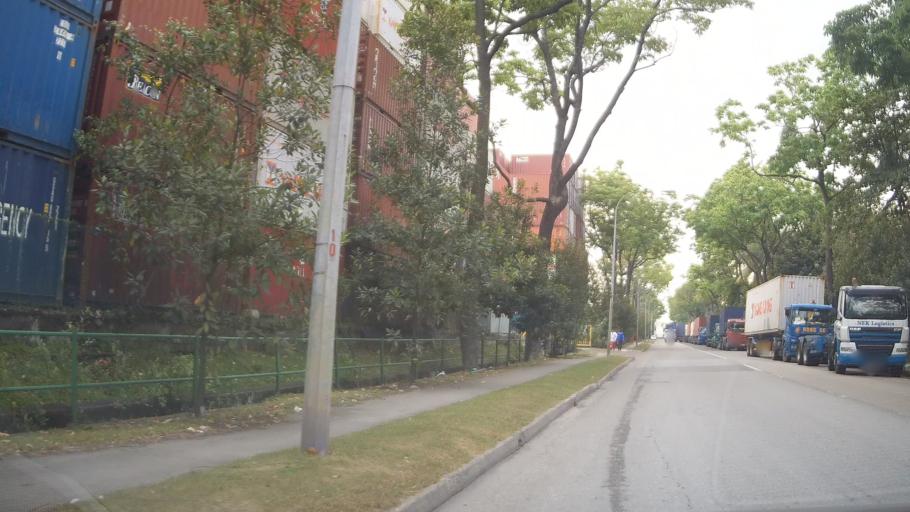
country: MY
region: Johor
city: Johor Bahru
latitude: 1.3197
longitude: 103.6434
